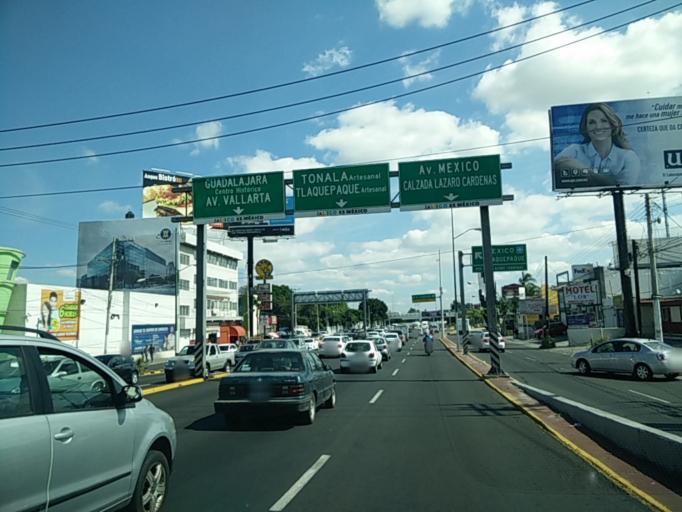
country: MX
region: Jalisco
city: Guadalajara
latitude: 20.6784
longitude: -103.4194
